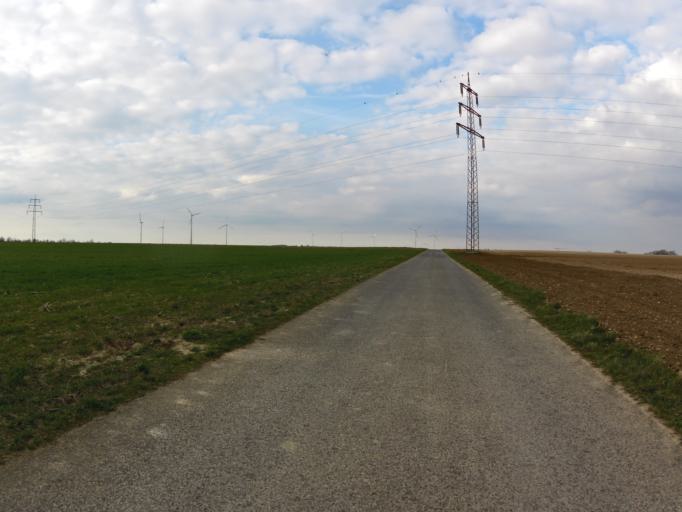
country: DE
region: Bavaria
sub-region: Regierungsbezirk Unterfranken
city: Buchbrunn
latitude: 49.7386
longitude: 10.1116
